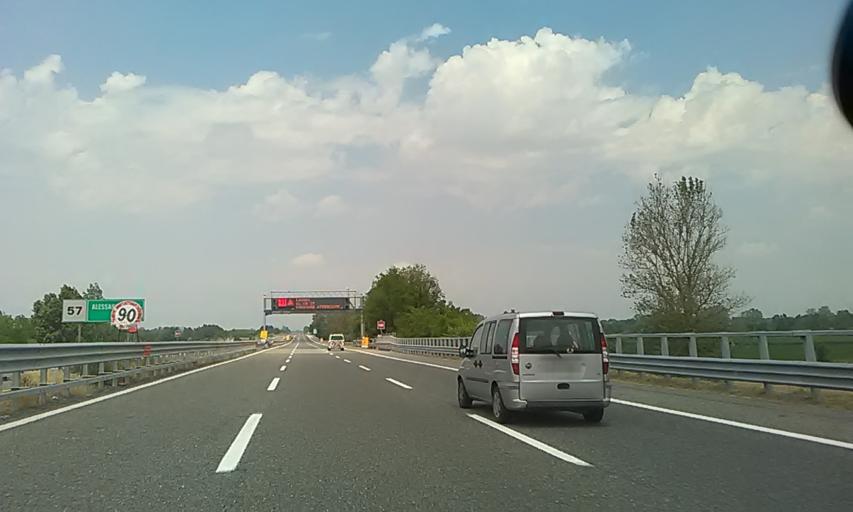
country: IT
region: Piedmont
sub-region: Provincia di Alessandria
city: Castellazzo Bormida
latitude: 44.8540
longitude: 8.5887
